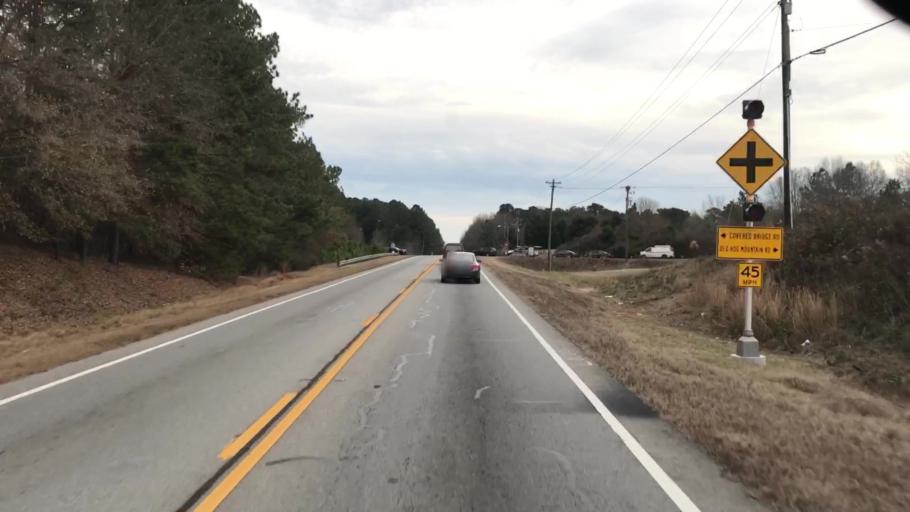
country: US
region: Georgia
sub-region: Jackson County
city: Hoschton
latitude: 34.0711
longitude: -83.7872
